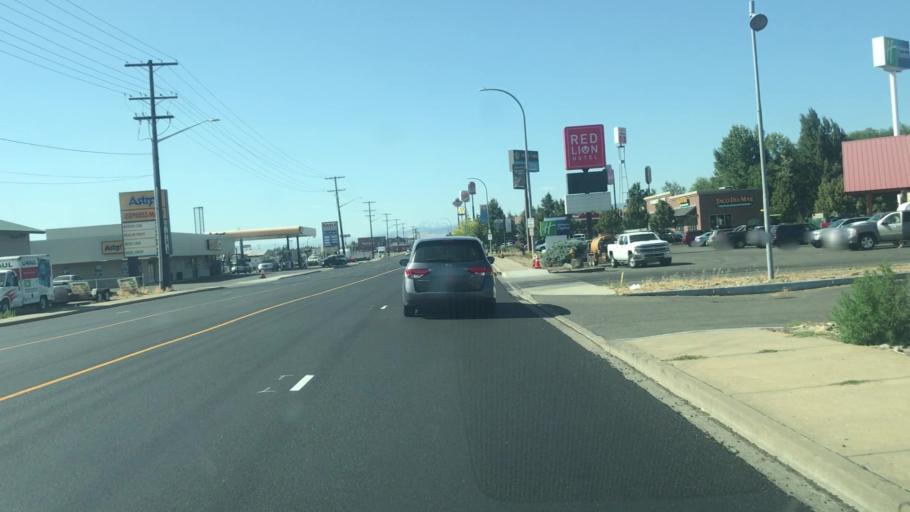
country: US
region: Washington
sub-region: Kittitas County
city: Ellensburg
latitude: 46.9757
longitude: -120.5420
